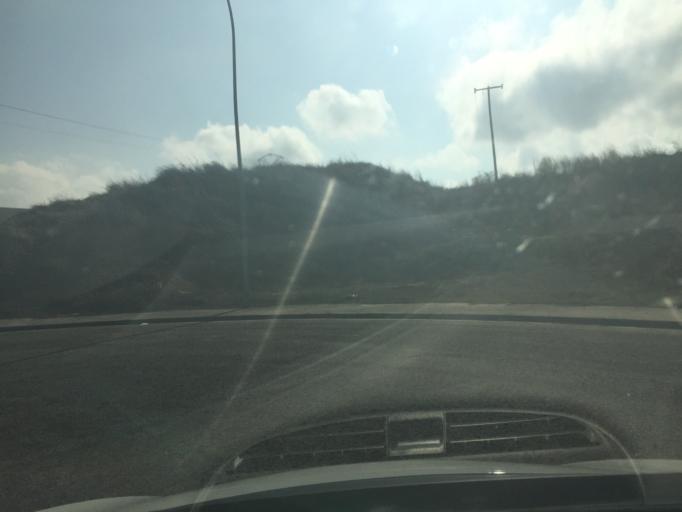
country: ES
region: Castille and Leon
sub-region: Provincia de Burgos
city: Medina de Pomar
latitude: 42.9249
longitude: -3.5850
